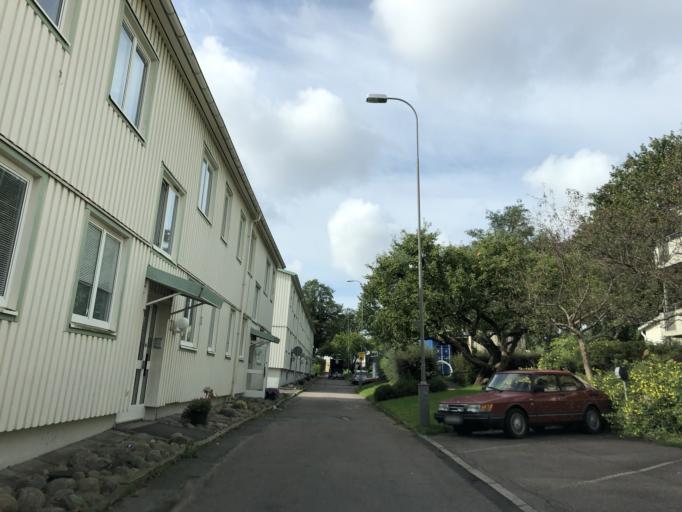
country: SE
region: Vaestra Goetaland
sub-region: Goteborg
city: Goeteborg
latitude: 57.7182
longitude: 12.0179
